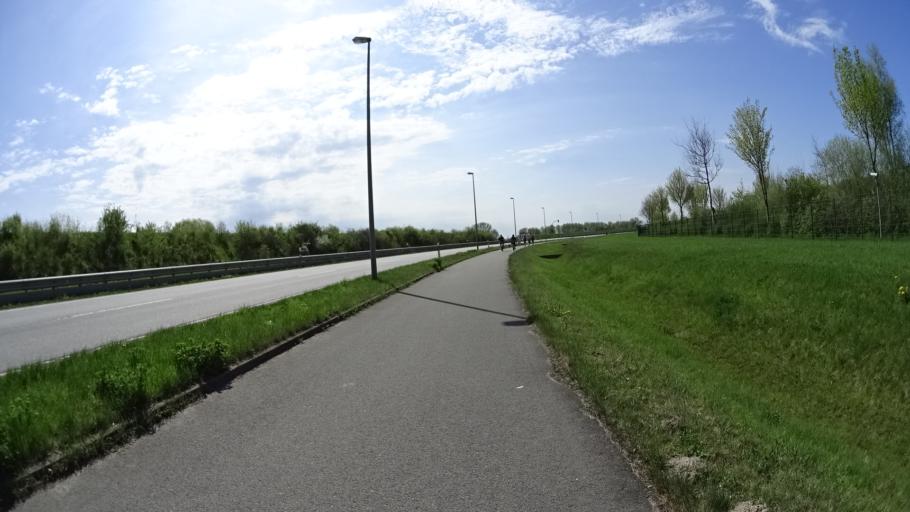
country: DE
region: Lower Saxony
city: Neu Wulmstorf
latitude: 53.5306
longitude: 9.8431
